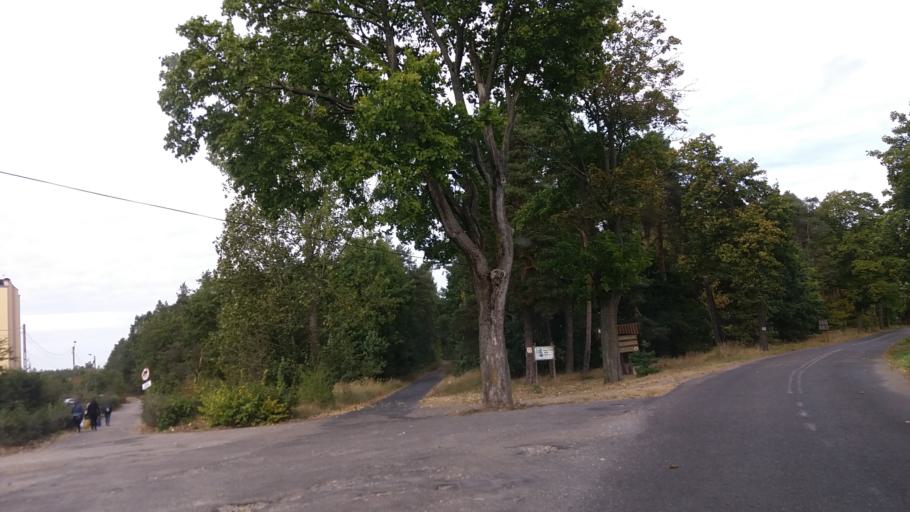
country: PL
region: Lubusz
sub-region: Powiat strzelecko-drezdenecki
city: Strzelce Krajenskie
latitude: 52.9592
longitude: 15.4542
